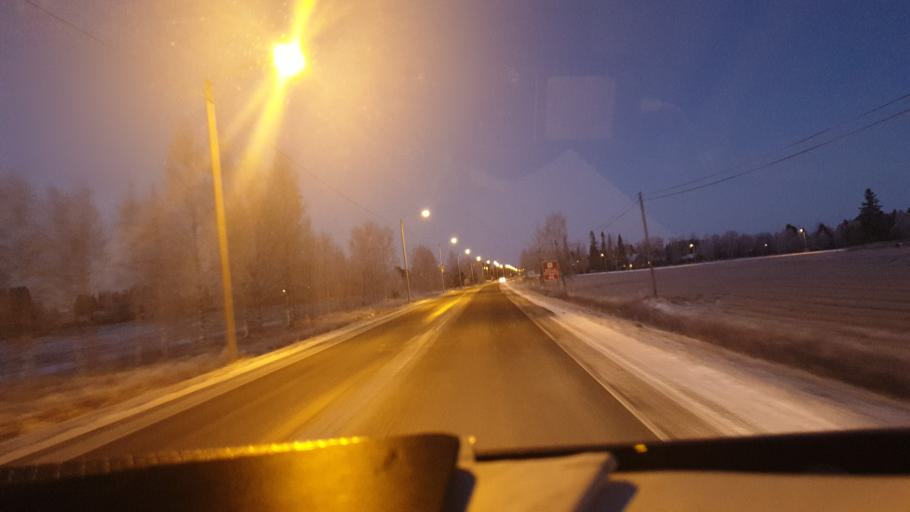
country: FI
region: Northern Ostrobothnia
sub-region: Raahe
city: Raahe
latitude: 64.6882
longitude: 24.6021
